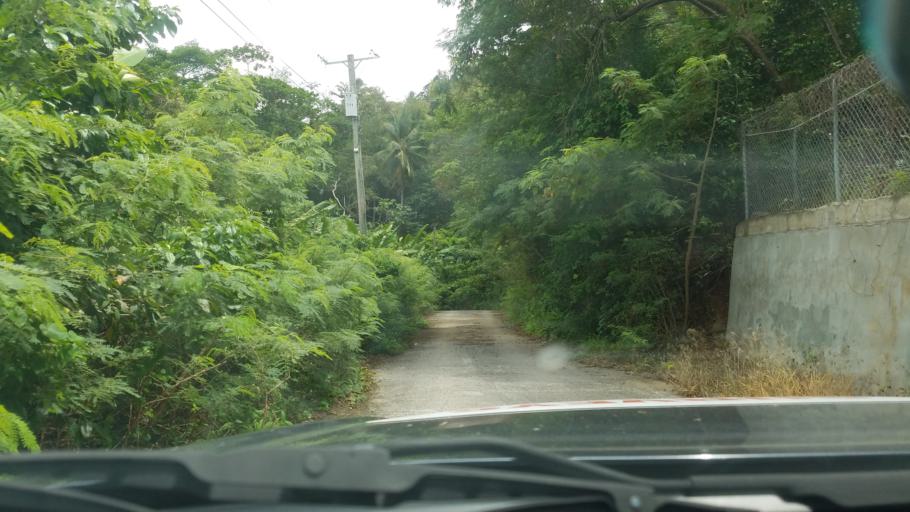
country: LC
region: Gros-Islet
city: Gros Islet
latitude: 14.0586
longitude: -60.9507
